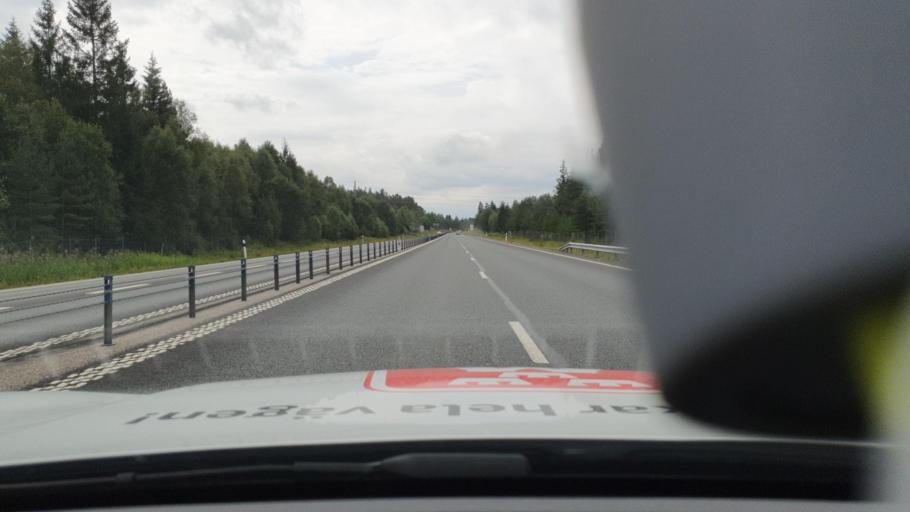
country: SE
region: Joenkoeping
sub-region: Gislaveds Kommun
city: Gislaved
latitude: 57.2883
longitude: 13.5127
